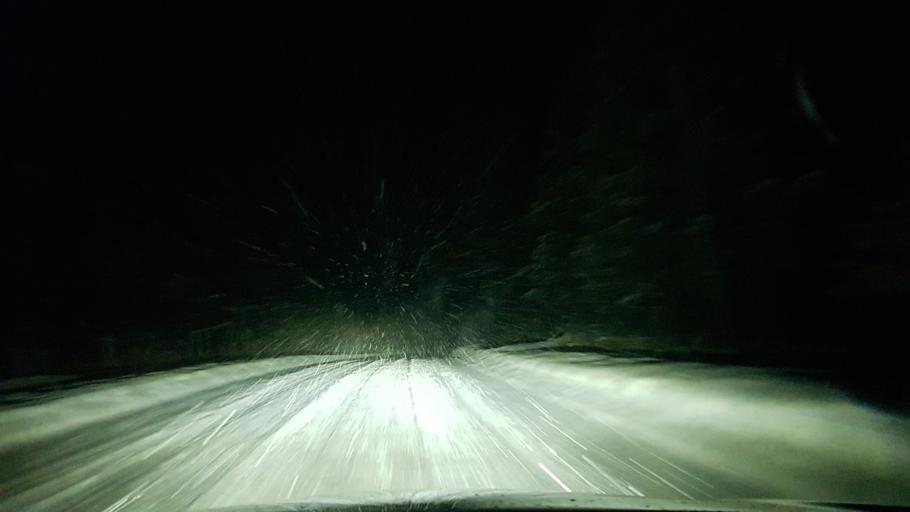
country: EE
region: Laeaene-Virumaa
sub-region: Tamsalu vald
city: Tamsalu
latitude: 59.2413
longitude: 26.1509
